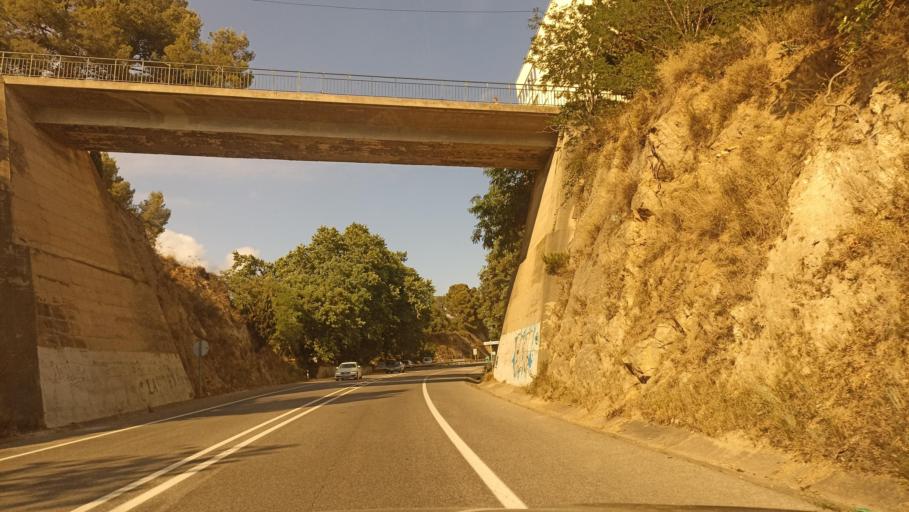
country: ES
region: Catalonia
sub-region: Provincia de Barcelona
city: Sant Pol de Mar
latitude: 41.6011
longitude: 2.6186
